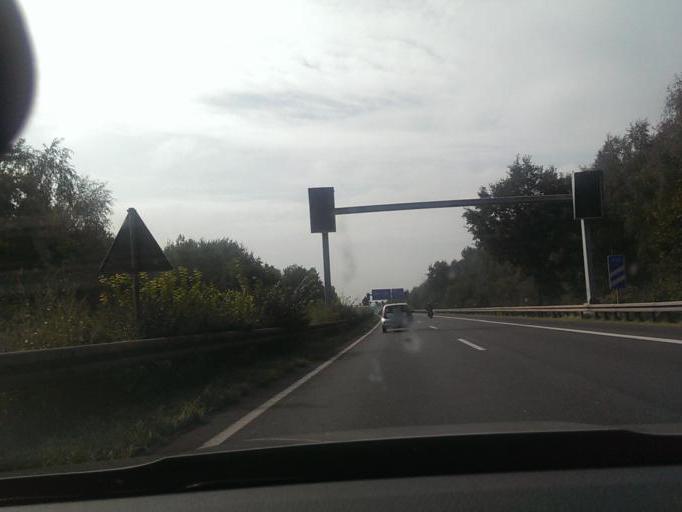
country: DE
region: Lower Saxony
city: Isernhagen Farster Bauerschaft
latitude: 52.4197
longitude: 9.8587
